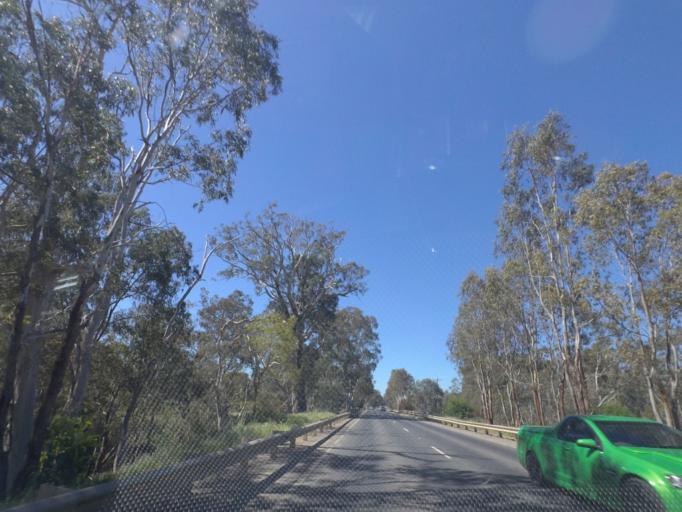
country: AU
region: Victoria
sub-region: Murrindindi
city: Kinglake West
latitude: -37.0256
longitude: 145.1110
